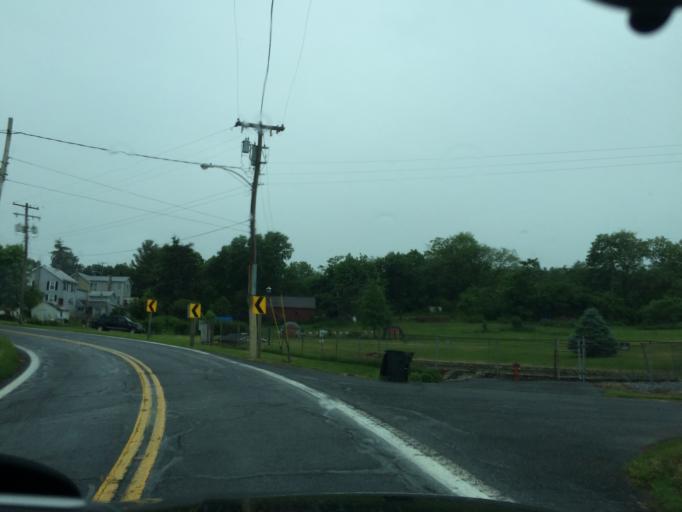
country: US
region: Maryland
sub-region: Frederick County
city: Thurmont
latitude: 39.6160
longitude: -77.3787
